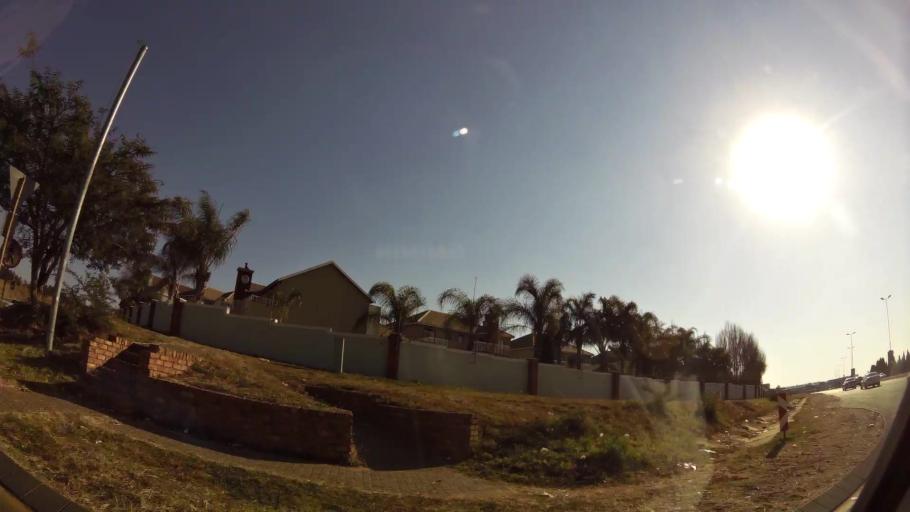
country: ZA
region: Gauteng
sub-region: City of Tshwane Metropolitan Municipality
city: Centurion
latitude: -25.8234
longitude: 28.3094
